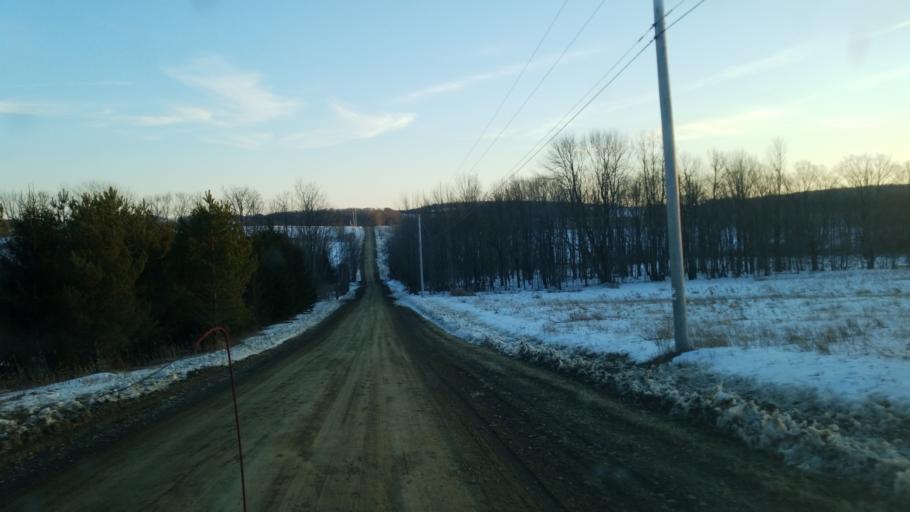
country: US
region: Pennsylvania
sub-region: Tioga County
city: Westfield
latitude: 42.0307
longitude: -77.6196
